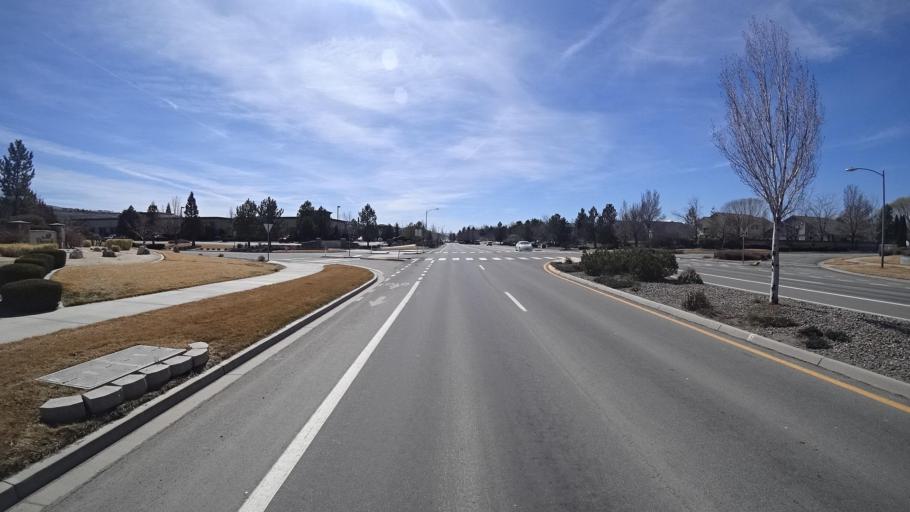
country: US
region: Nevada
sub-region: Washoe County
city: Sun Valley
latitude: 39.5821
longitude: -119.7241
